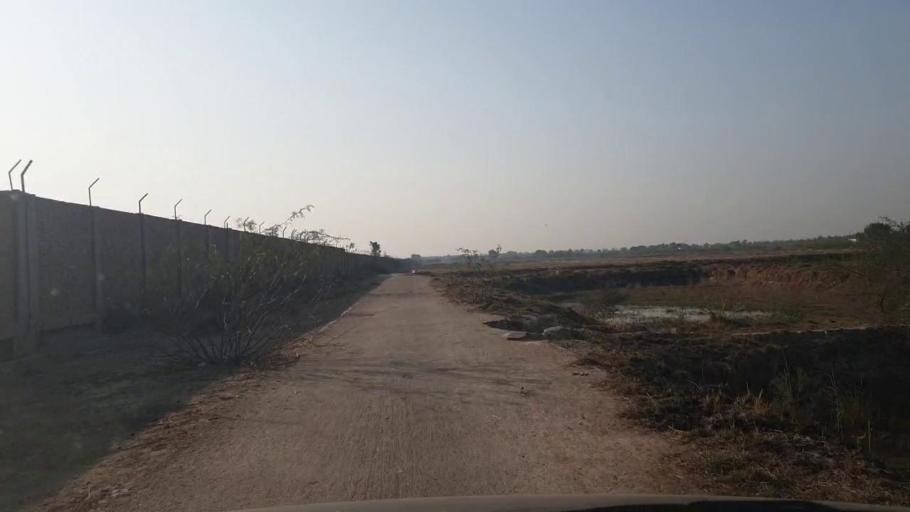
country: PK
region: Sindh
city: Tando Adam
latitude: 25.7472
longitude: 68.6400
